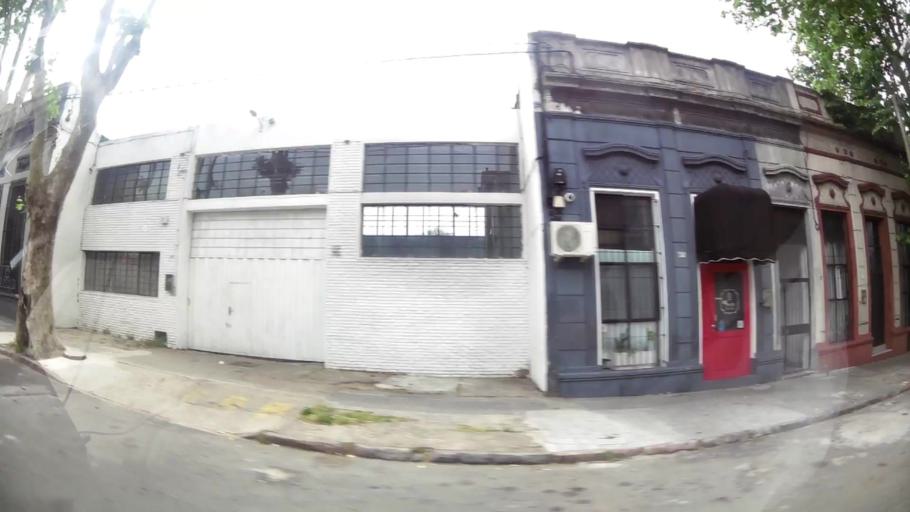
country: UY
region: Montevideo
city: Montevideo
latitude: -34.8947
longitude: -56.1713
